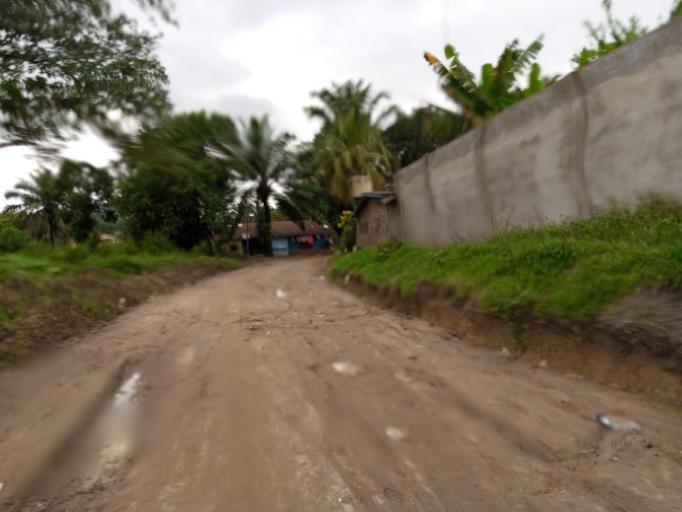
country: SL
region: Eastern Province
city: Kenema
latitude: 7.8584
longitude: -11.1978
